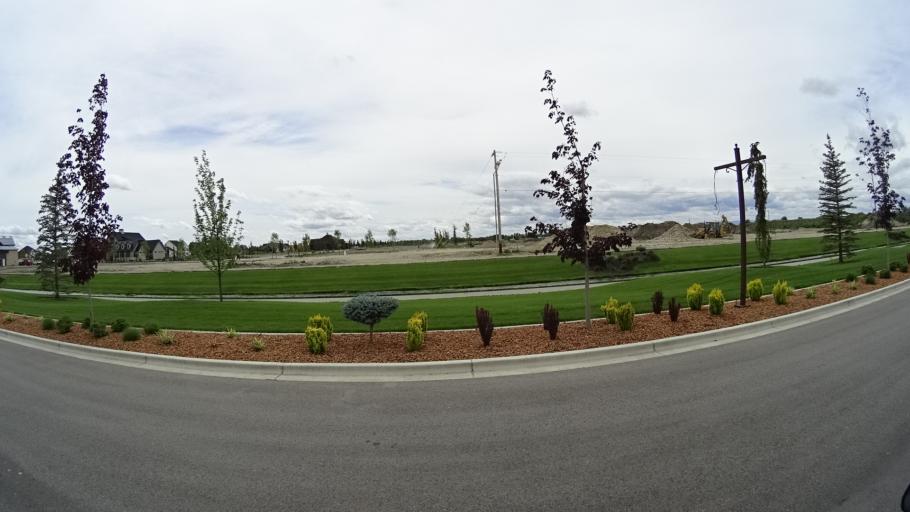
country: US
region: Idaho
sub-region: Ada County
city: Star
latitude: 43.7030
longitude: -116.4409
